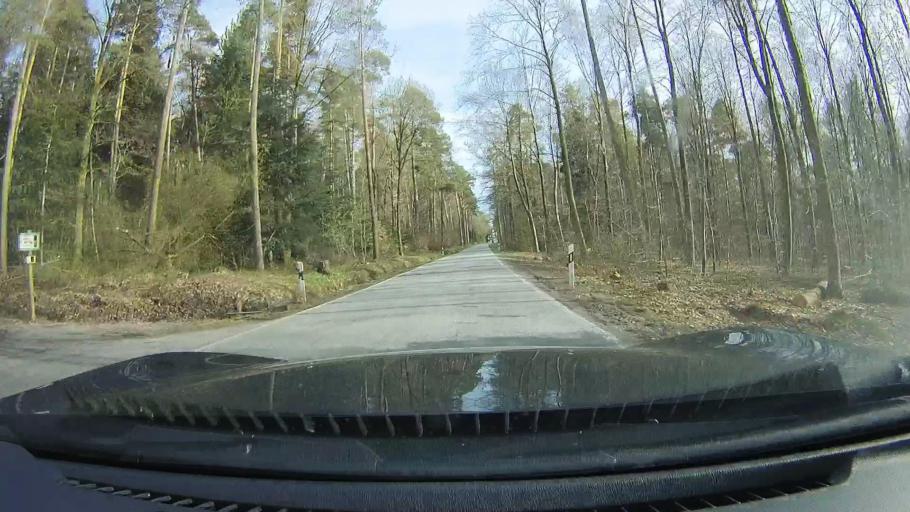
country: DE
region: Baden-Wuerttemberg
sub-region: Karlsruhe Region
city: Walldurn
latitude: 49.6216
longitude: 9.3282
